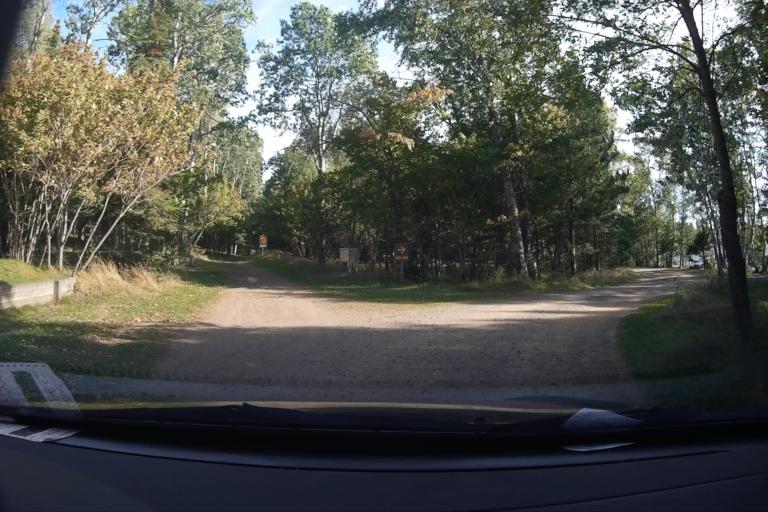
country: CA
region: Ontario
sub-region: Thunder Bay District
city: Thunder Bay
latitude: 48.3704
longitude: -88.8064
